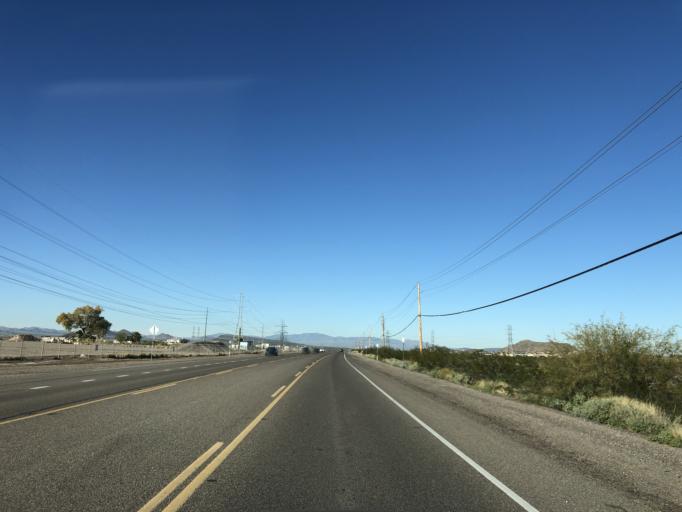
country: US
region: Arizona
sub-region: Maricopa County
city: Sun City West
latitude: 33.6985
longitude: -112.2898
